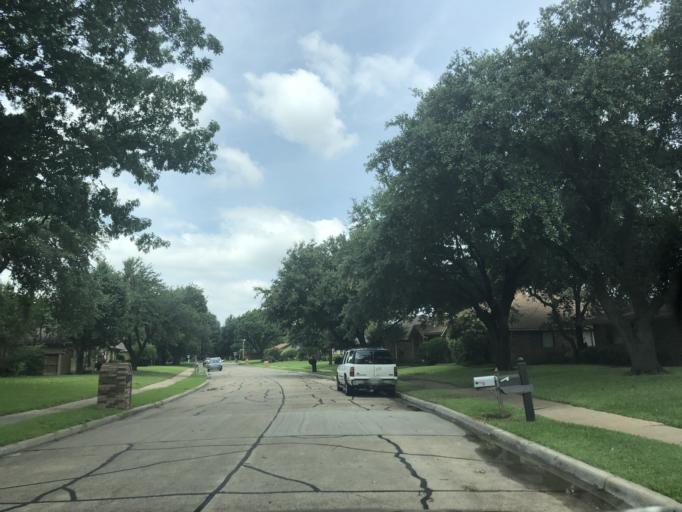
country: US
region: Texas
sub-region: Dallas County
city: Garland
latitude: 32.8511
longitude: -96.6193
